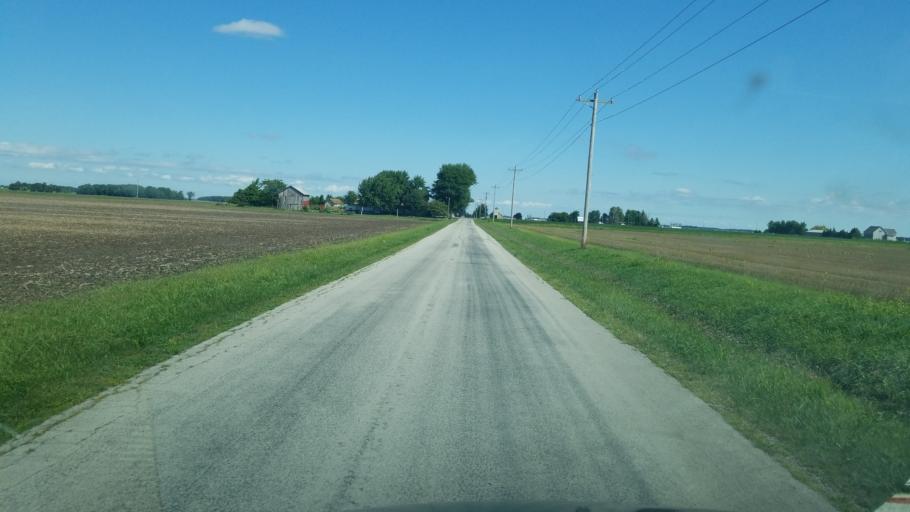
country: US
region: Ohio
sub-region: Hancock County
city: McComb
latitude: 41.1478
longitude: -83.7462
